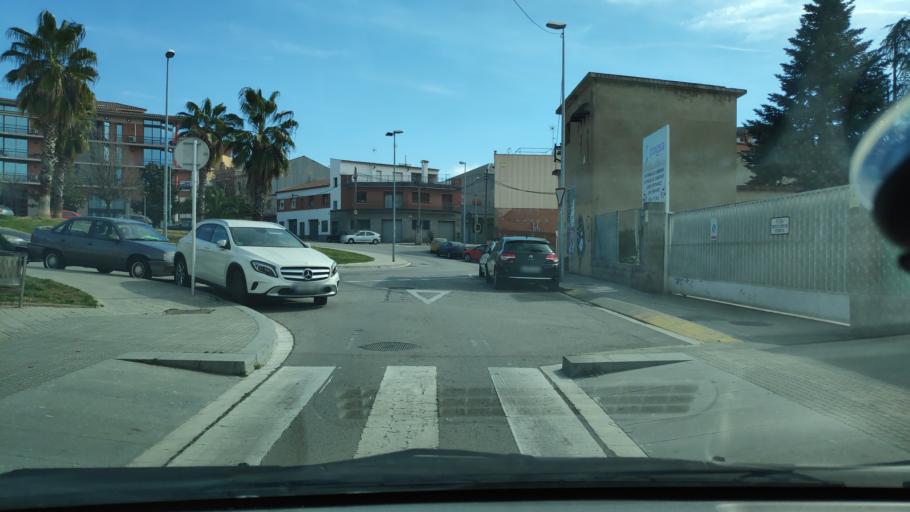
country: ES
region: Catalonia
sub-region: Provincia de Barcelona
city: Rubi
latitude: 41.4974
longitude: 2.0346
